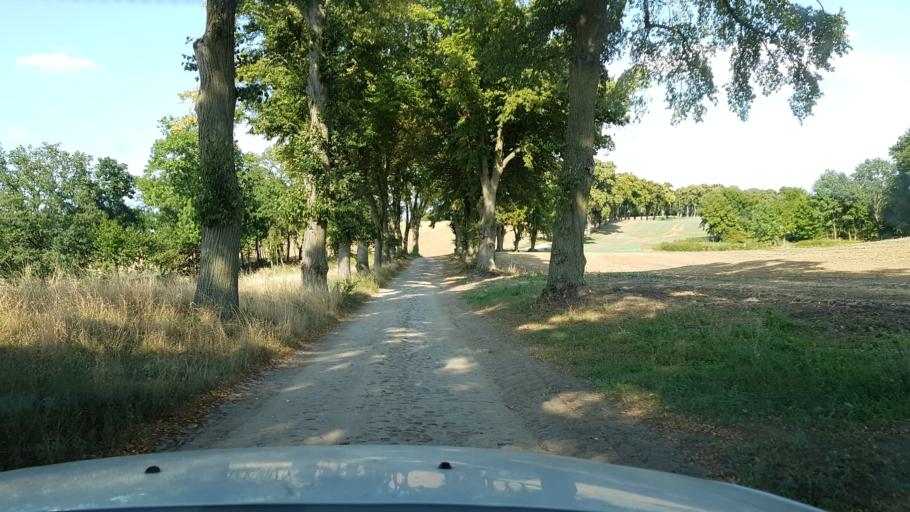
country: PL
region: West Pomeranian Voivodeship
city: Trzcinsko Zdroj
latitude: 52.9064
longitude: 14.5817
